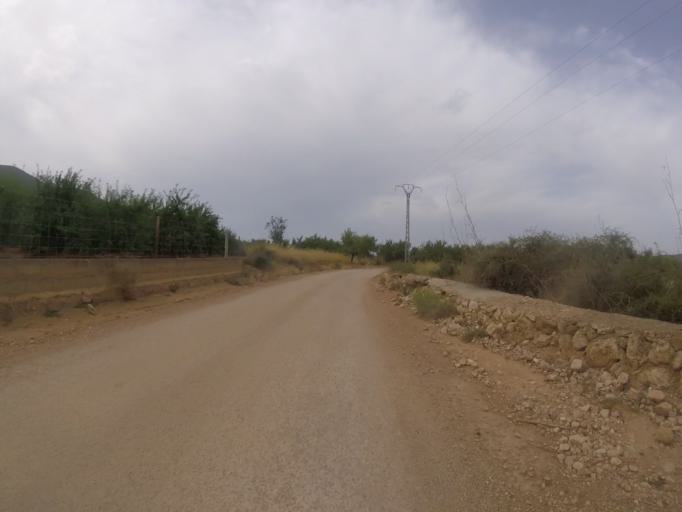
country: ES
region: Valencia
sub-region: Provincia de Castello
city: Alcoceber
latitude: 40.2734
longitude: 0.2574
